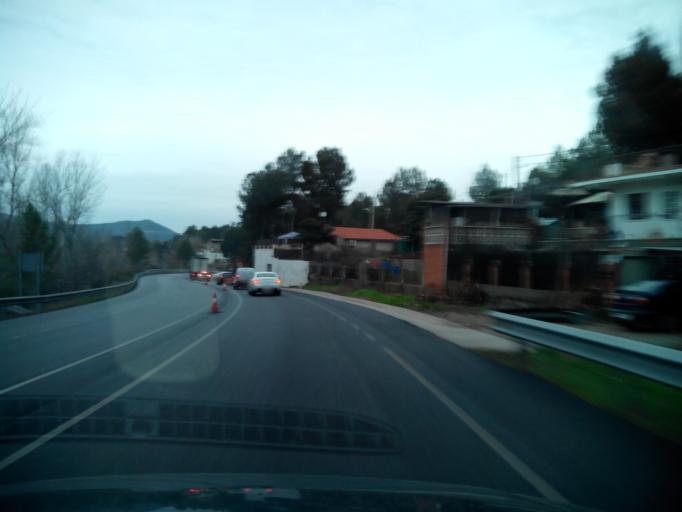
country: ES
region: Catalonia
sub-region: Provincia de Barcelona
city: Monistrol de Montserrat
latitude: 41.6111
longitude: 1.8742
